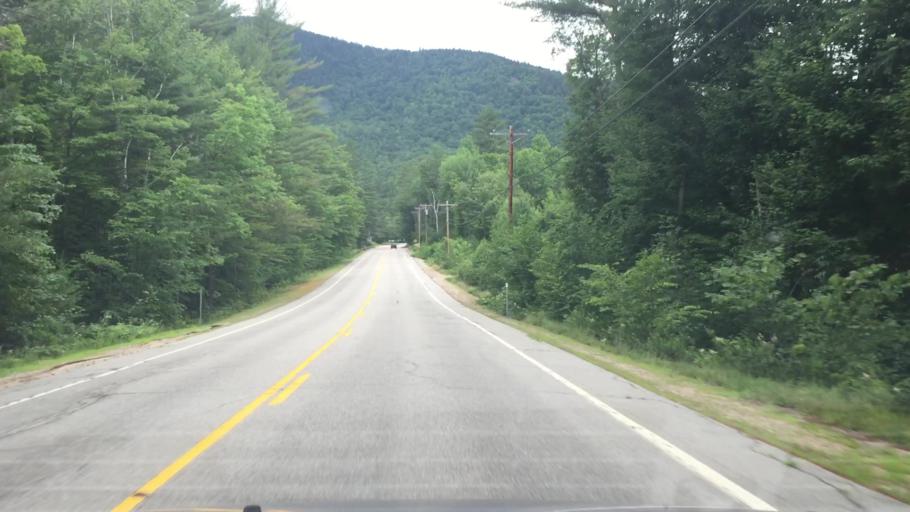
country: US
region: New Hampshire
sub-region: Carroll County
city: North Conway
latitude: 44.0750
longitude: -71.2971
